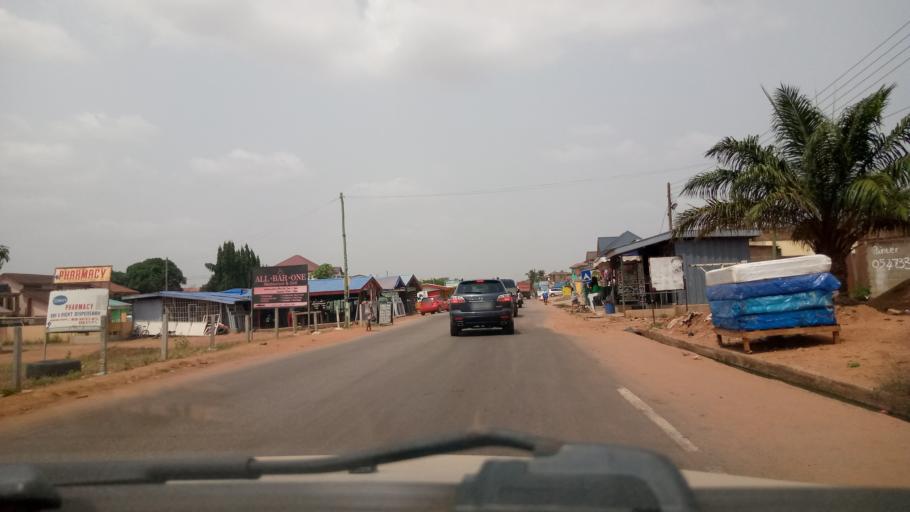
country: GH
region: Greater Accra
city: Medina Estates
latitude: 5.6867
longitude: -0.1860
